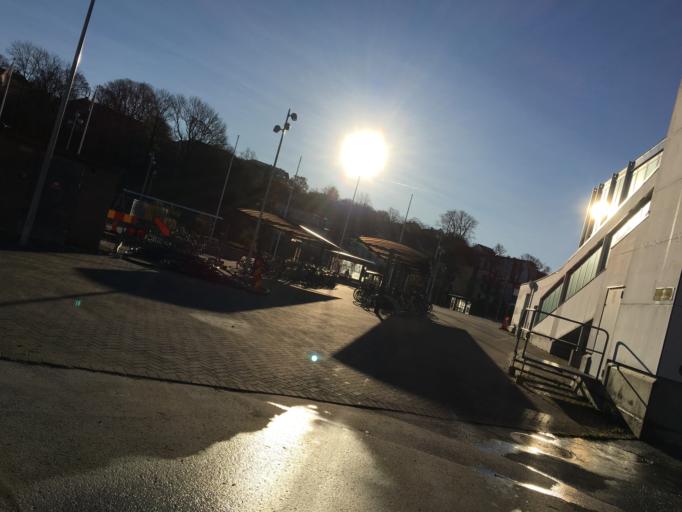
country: SE
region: Gotland
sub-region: Gotland
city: Visby
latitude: 57.6348
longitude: 18.2806
